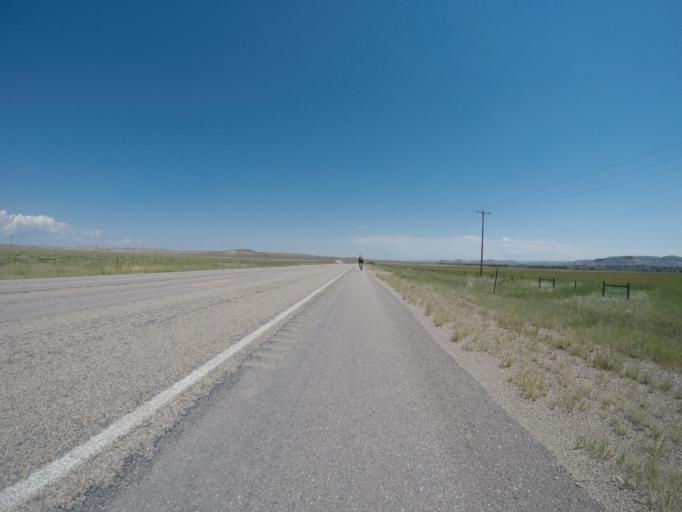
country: US
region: Wyoming
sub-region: Sublette County
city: Marbleton
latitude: 42.4187
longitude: -110.1132
